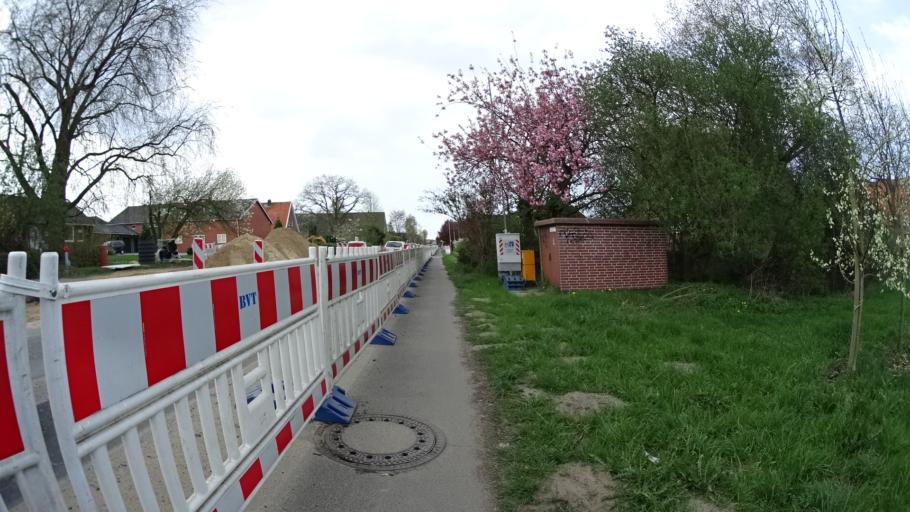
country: DE
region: Lower Saxony
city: Jork
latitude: 53.5264
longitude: 9.7058
